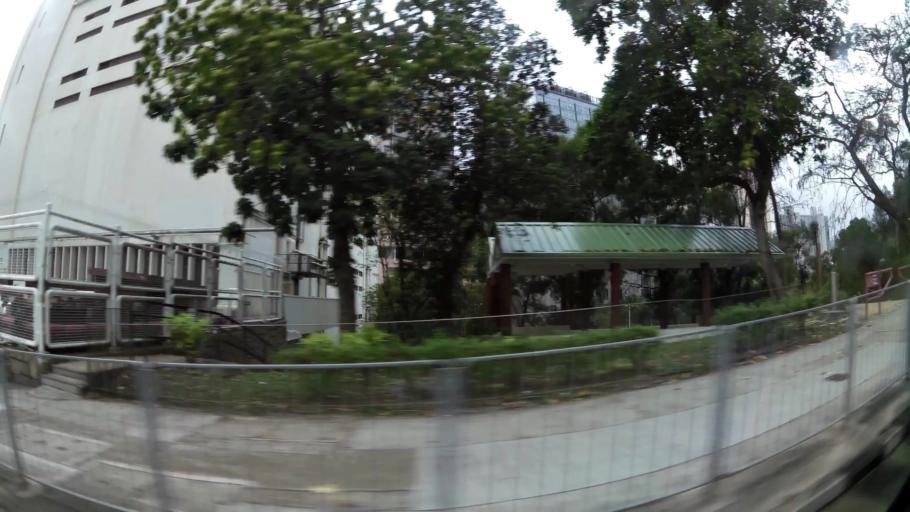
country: HK
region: Tsuen Wan
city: Tsuen Wan
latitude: 22.3716
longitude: 114.1305
